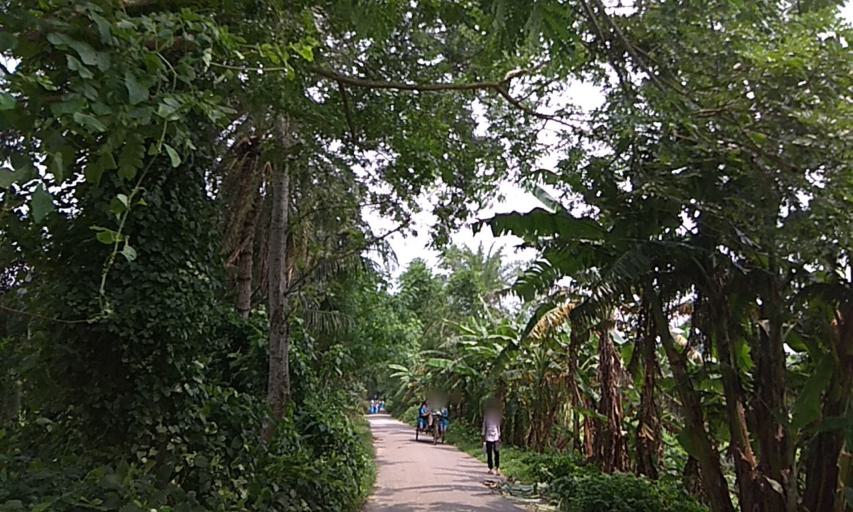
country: BD
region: Dhaka
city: Faridpur
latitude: 23.5365
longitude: 89.9684
